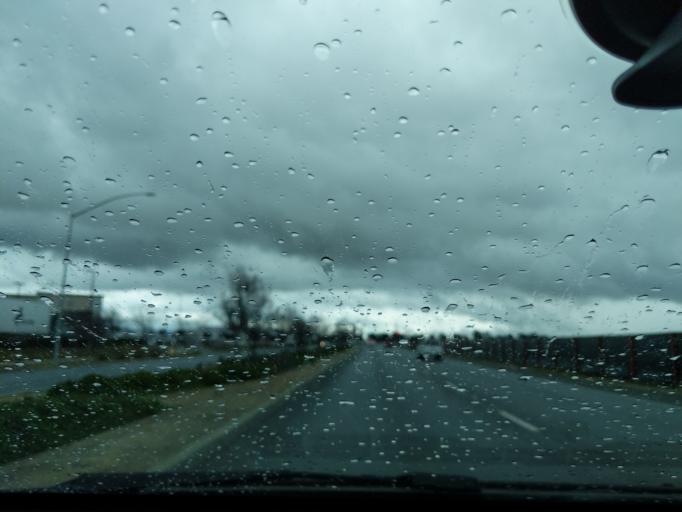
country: US
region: California
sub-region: Monterey County
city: Boronda
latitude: 36.7165
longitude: -121.6661
